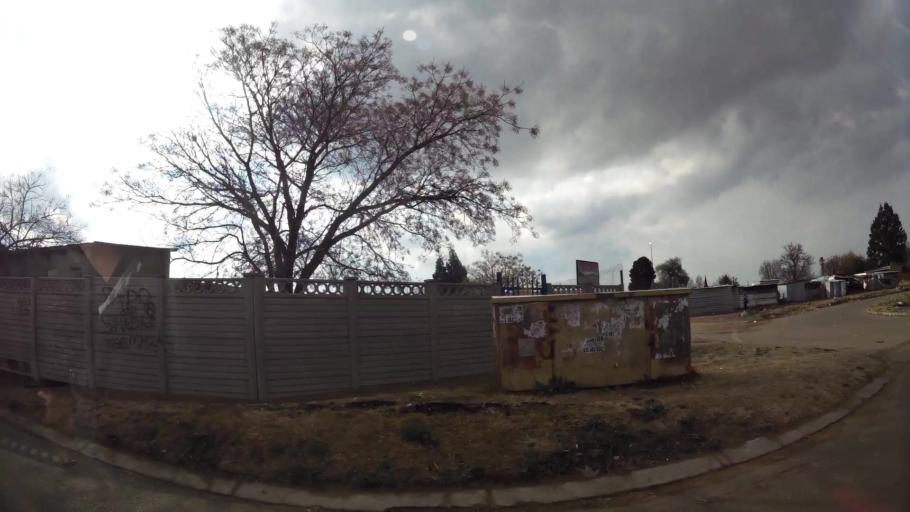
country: ZA
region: Orange Free State
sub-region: Fezile Dabi District Municipality
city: Sasolburg
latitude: -26.8398
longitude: 27.8477
